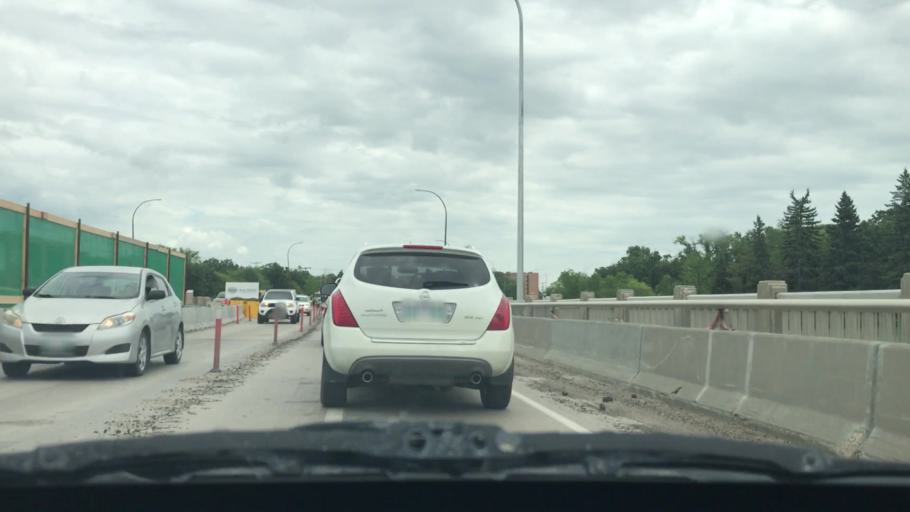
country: CA
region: Manitoba
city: Winnipeg
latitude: 49.8579
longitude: -97.0950
